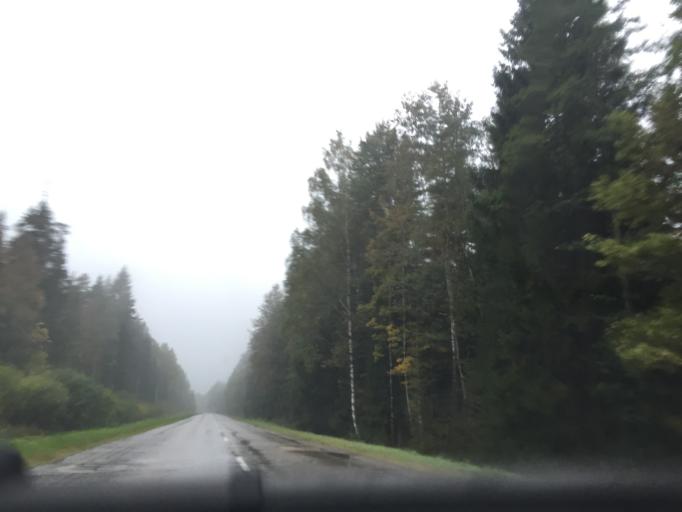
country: LV
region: Ropazu
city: Ropazi
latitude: 56.9863
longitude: 24.6356
